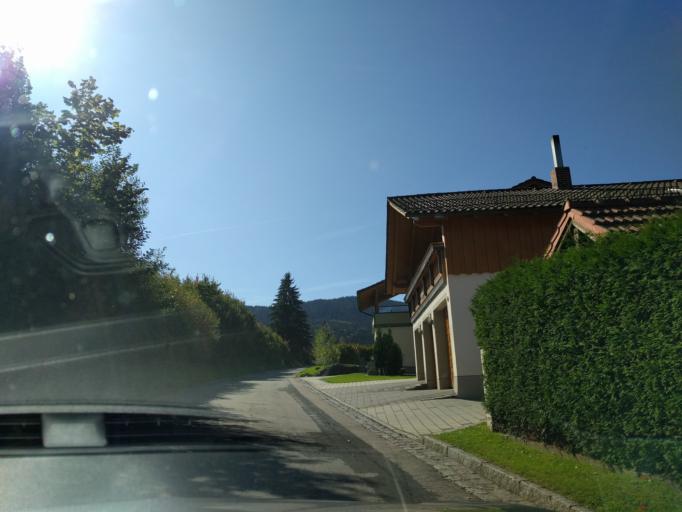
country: DE
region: Bavaria
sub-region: Upper Palatinate
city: Hohenwarth
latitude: 49.2010
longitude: 12.9317
